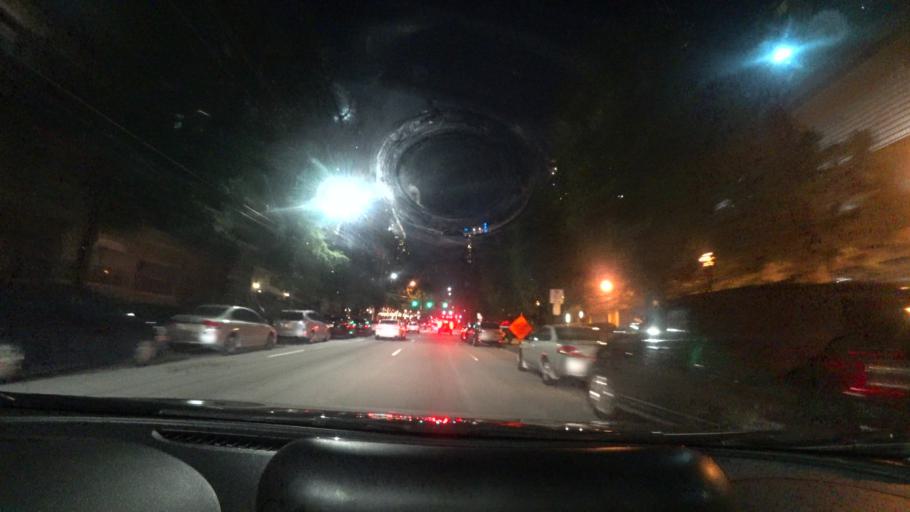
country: US
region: Georgia
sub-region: Fulton County
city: Atlanta
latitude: 33.7803
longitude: -84.3827
